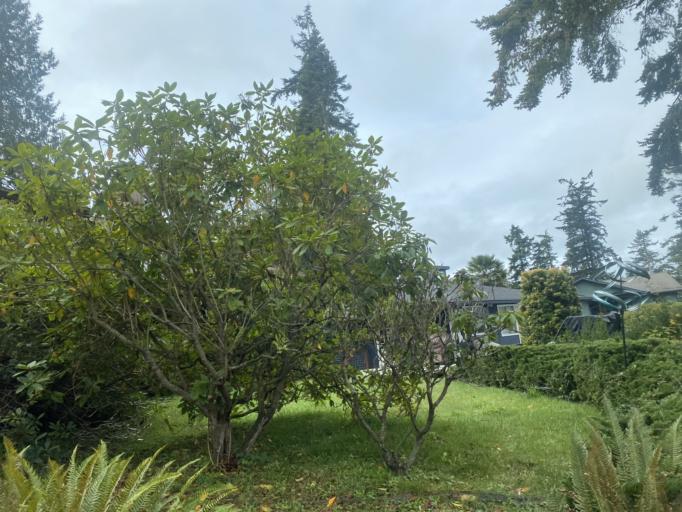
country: US
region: Washington
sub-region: Island County
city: Camano
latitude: 48.0944
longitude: -122.4922
